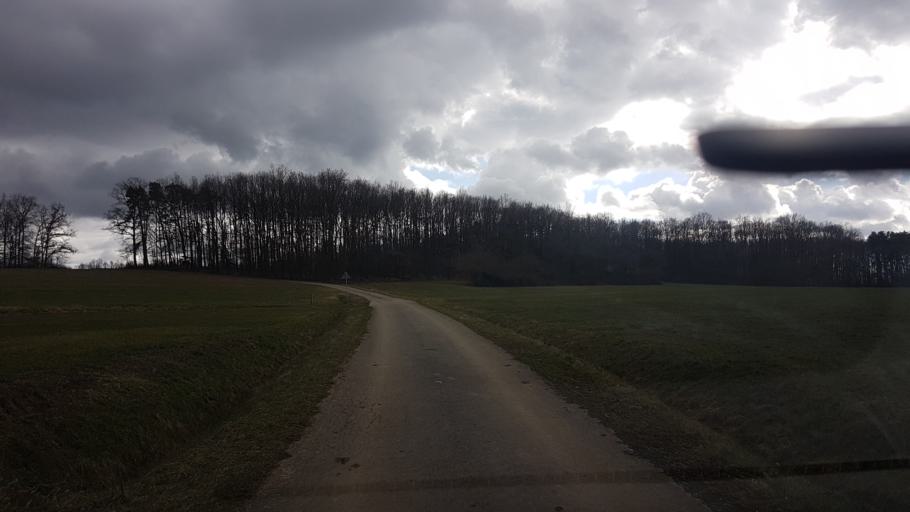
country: DE
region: Bavaria
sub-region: Upper Franconia
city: Hirschaid
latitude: 49.7920
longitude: 10.9722
